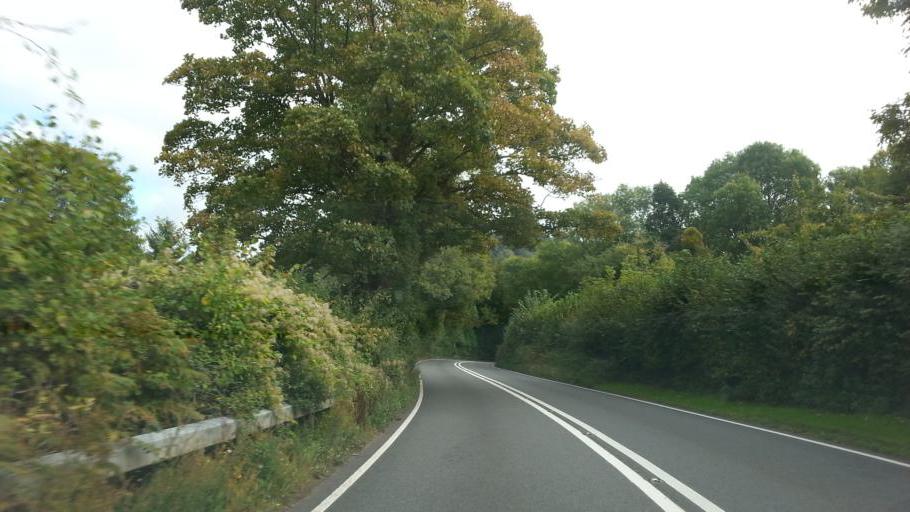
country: GB
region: England
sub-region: Gloucestershire
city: Mitcheldean
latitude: 51.8774
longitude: -2.4341
